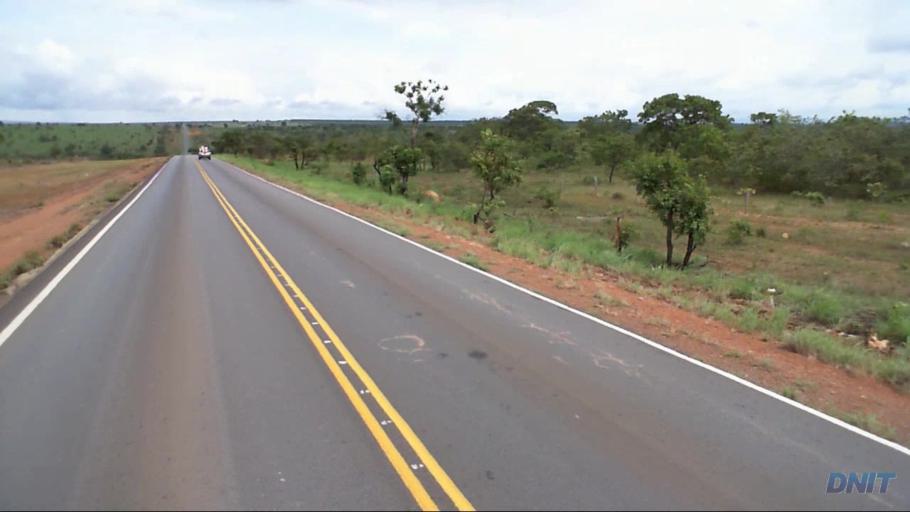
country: BR
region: Goias
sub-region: Padre Bernardo
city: Padre Bernardo
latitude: -15.3005
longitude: -48.2332
